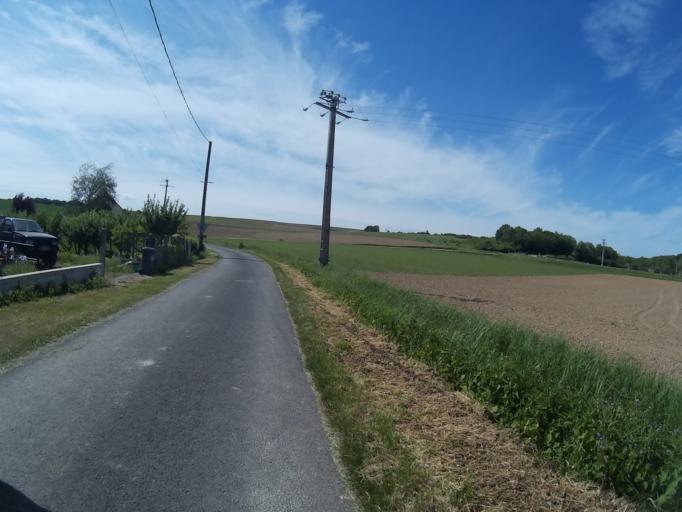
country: FR
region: Centre
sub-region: Departement du Loir-et-Cher
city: Lunay
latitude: 47.8103
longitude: 0.9545
